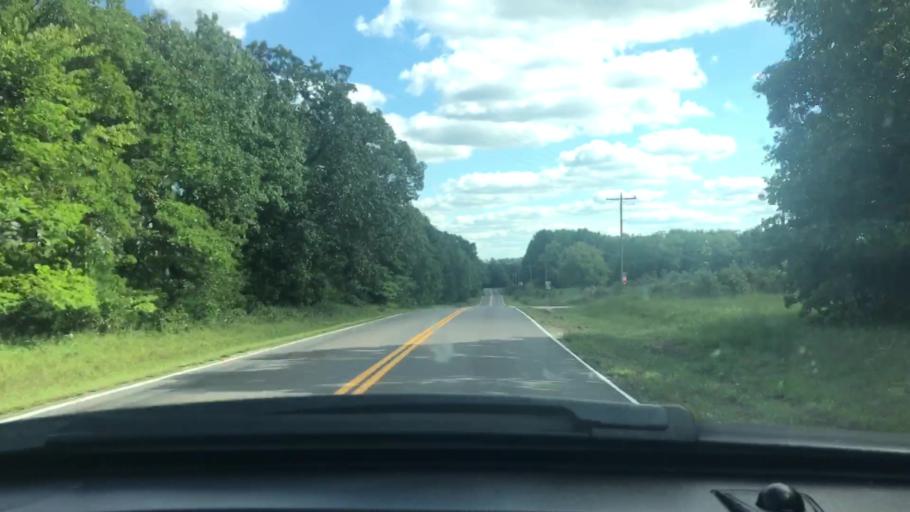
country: US
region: Missouri
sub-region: Wright County
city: Hartville
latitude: 37.3600
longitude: -92.3433
